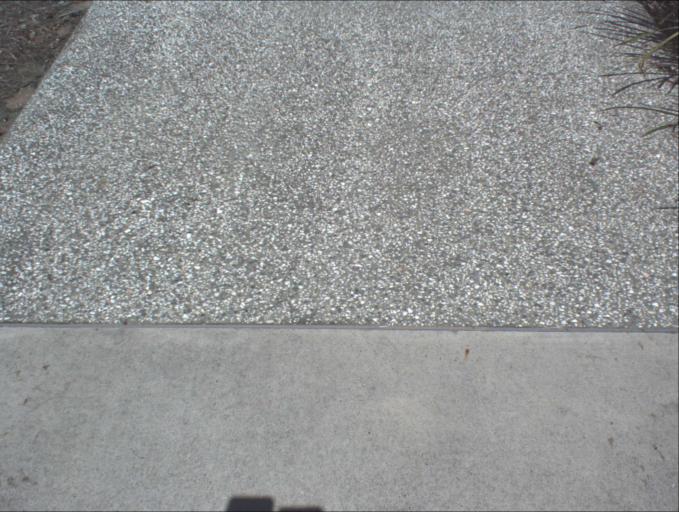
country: AU
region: Queensland
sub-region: Logan
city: North Maclean
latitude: -27.8034
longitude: 152.9543
